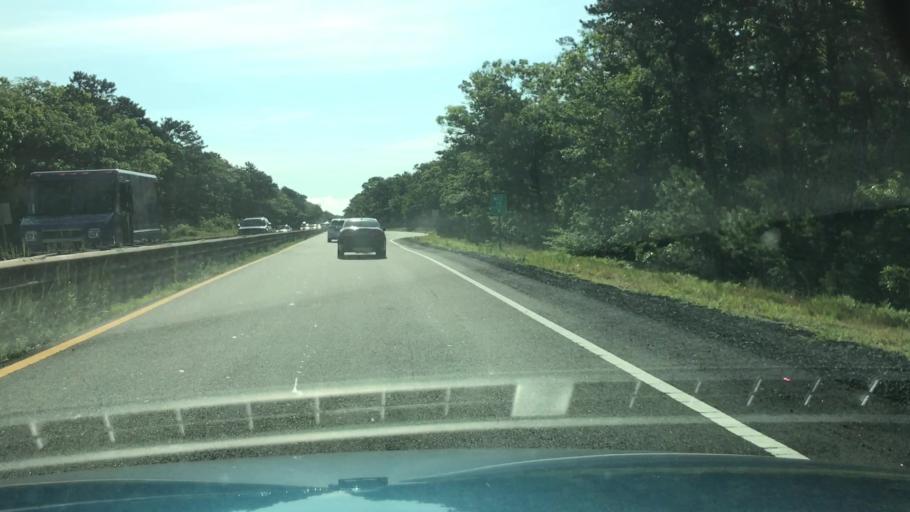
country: US
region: Massachusetts
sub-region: Barnstable County
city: South Dennis
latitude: 41.7002
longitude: -70.1389
